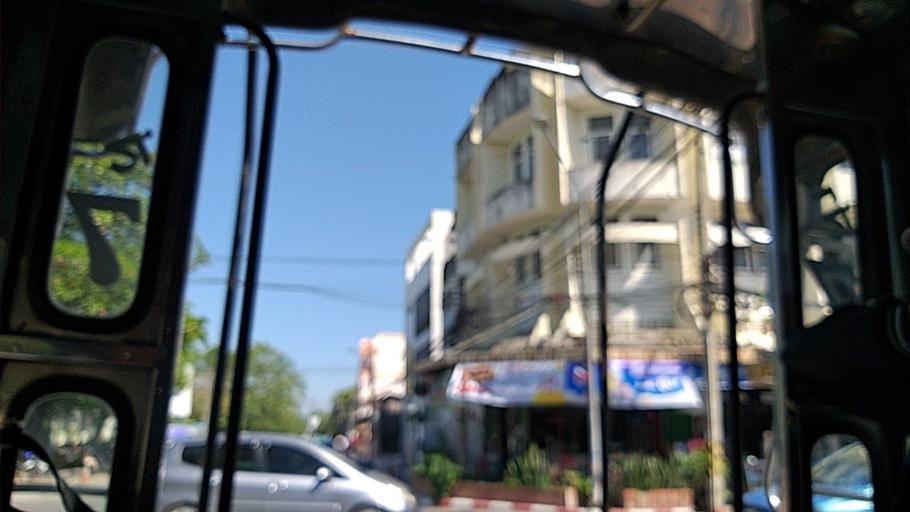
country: TH
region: Nakhon Ratchasima
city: Nakhon Ratchasima
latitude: 14.9792
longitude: 102.1006
